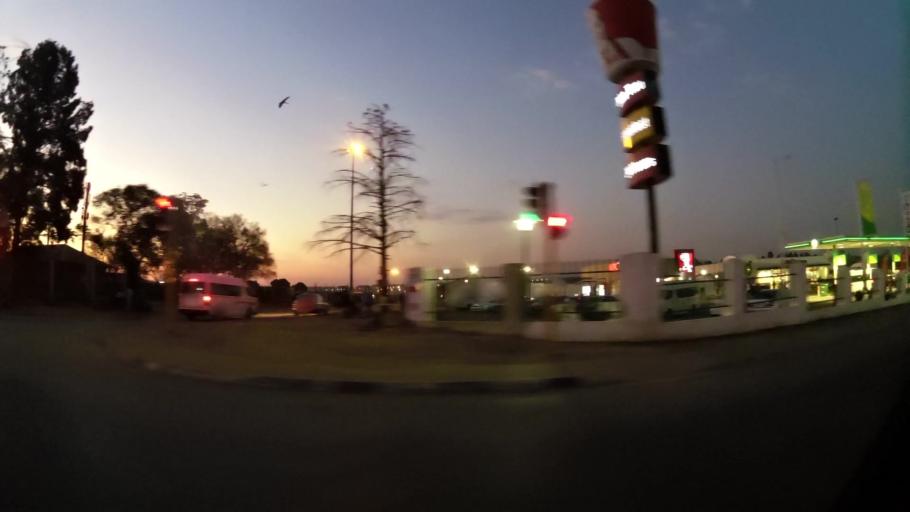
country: ZA
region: Gauteng
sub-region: City of Johannesburg Metropolitan Municipality
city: Roodepoort
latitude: -26.2189
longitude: 27.9165
